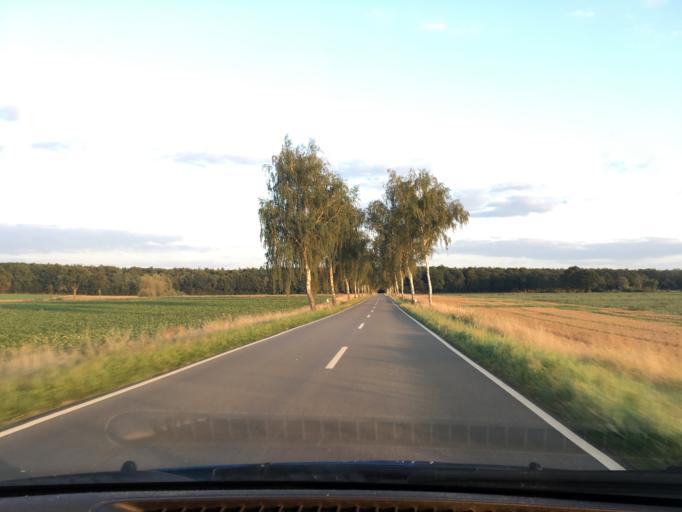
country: DE
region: Lower Saxony
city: Tosterglope
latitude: 53.2364
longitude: 10.7933
